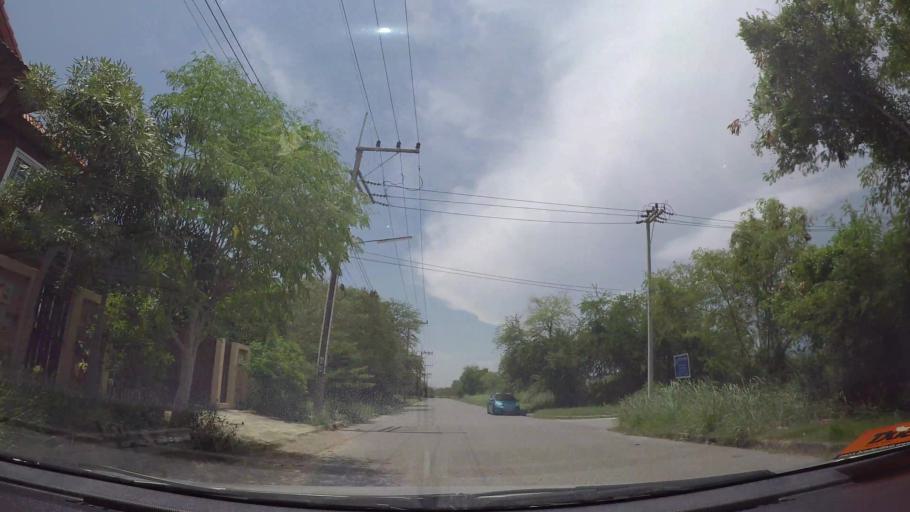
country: TH
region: Chon Buri
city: Chon Buri
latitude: 13.3434
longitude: 100.9540
